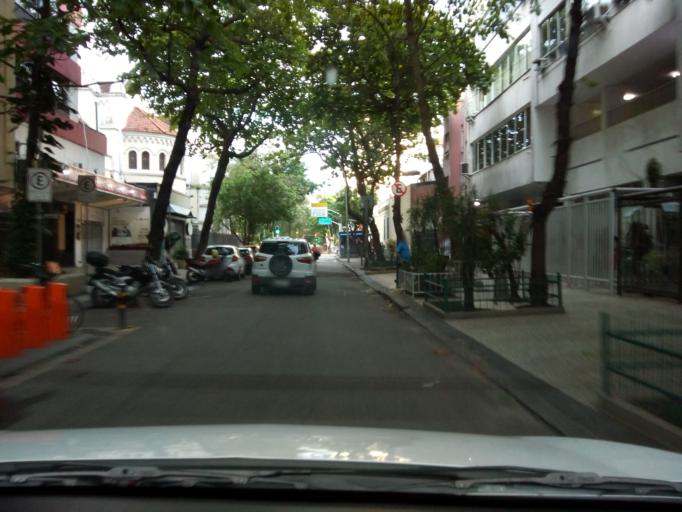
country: BR
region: Rio de Janeiro
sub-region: Rio De Janeiro
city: Rio de Janeiro
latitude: -22.9852
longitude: -43.2049
